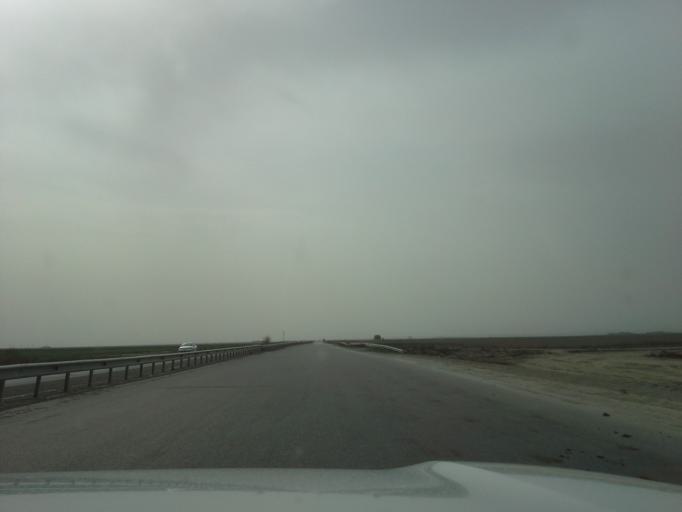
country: TM
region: Ahal
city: Kaka
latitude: 37.4633
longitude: 59.5057
